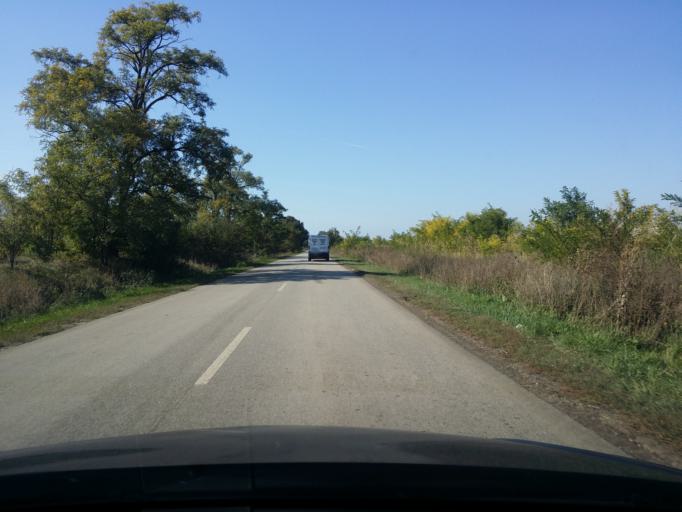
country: HU
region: Jasz-Nagykun-Szolnok
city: Ocsod
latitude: 46.9897
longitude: 20.3642
